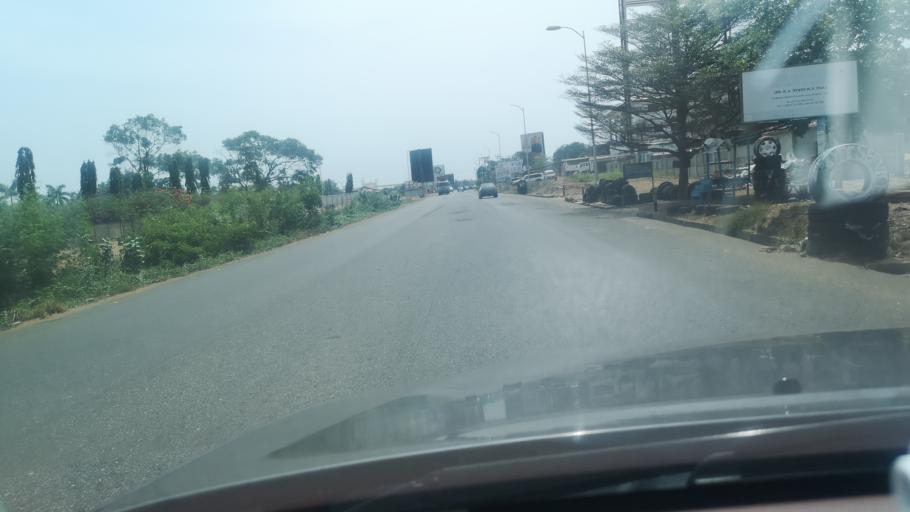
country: GH
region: Greater Accra
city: Nungua
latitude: 5.6153
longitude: -0.0682
